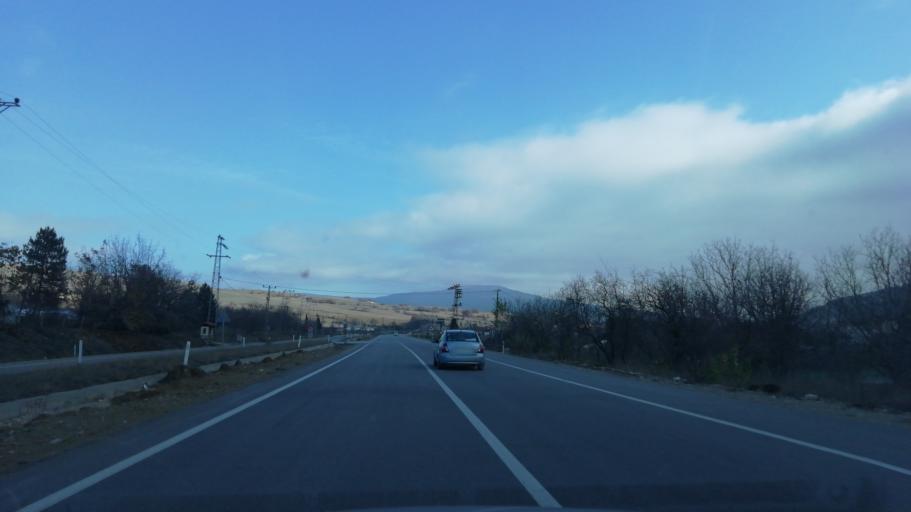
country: TR
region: Karabuk
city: Safranbolu
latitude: 41.2172
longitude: 32.7384
